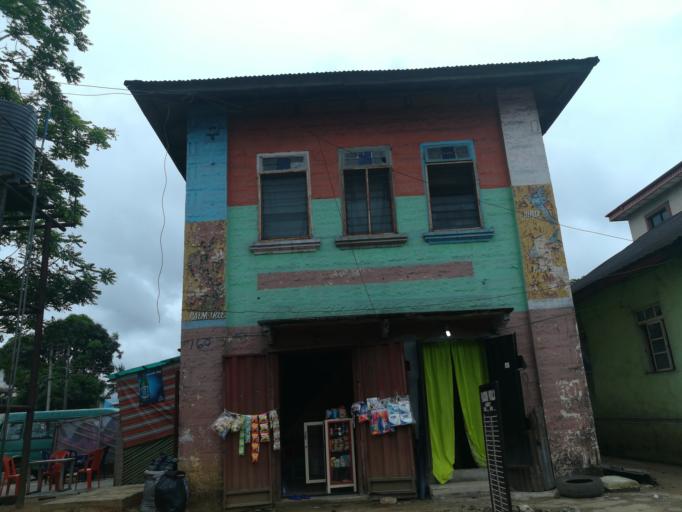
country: NG
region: Rivers
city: Port Harcourt
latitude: 4.7612
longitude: 7.0287
